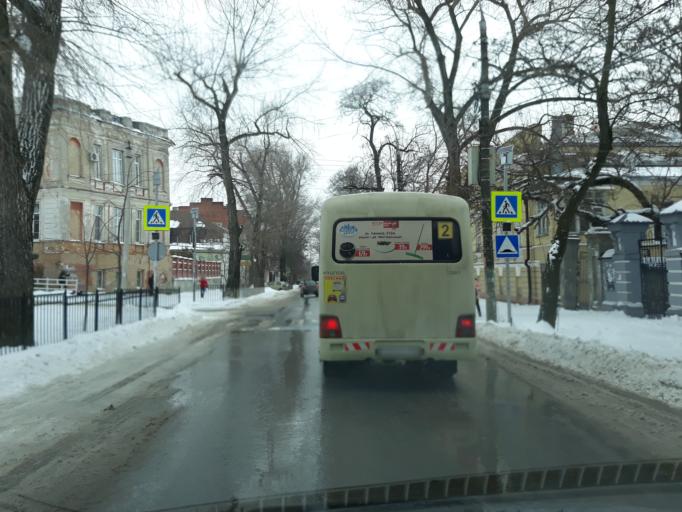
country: RU
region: Rostov
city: Taganrog
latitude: 47.2145
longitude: 38.9335
